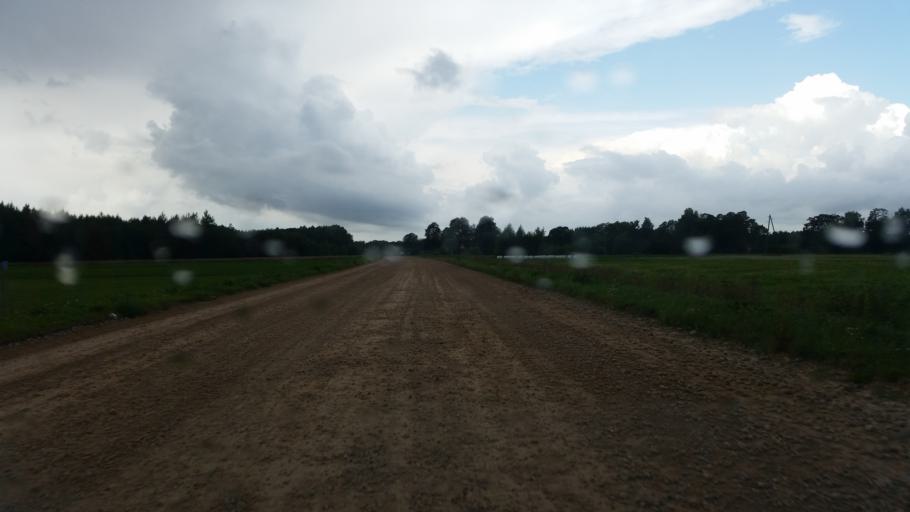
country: LV
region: Vecumnieki
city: Vecumnieki
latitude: 56.4301
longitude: 24.4552
